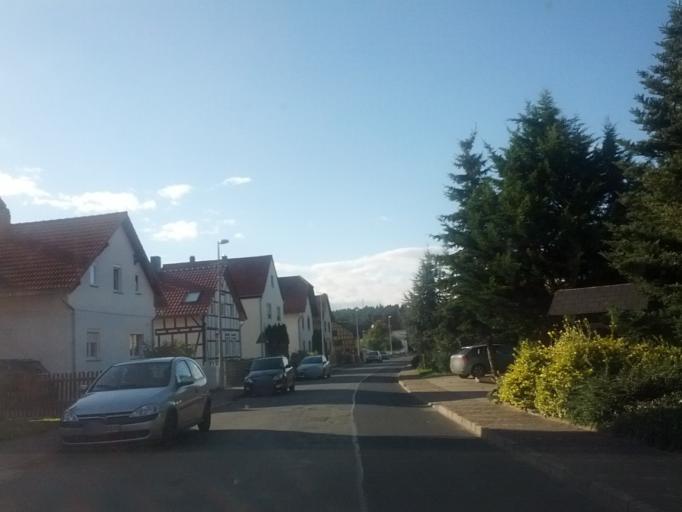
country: DE
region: Thuringia
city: Lauchroden
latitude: 50.9641
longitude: 10.1605
